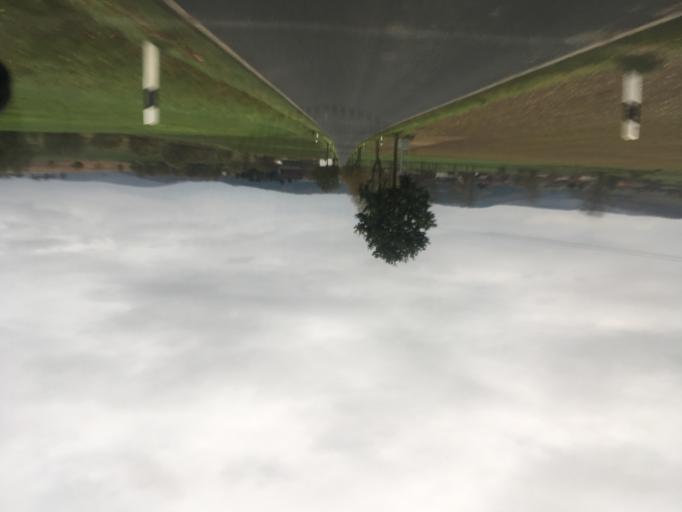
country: DE
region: Lower Saxony
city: Uslar
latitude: 51.6734
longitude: 9.6469
